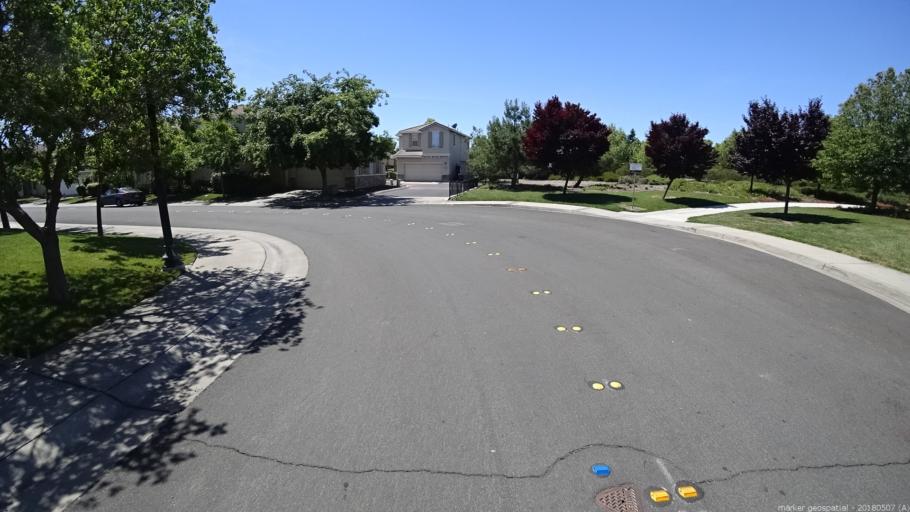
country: US
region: California
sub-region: Sacramento County
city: Elverta
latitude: 38.6731
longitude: -121.5169
